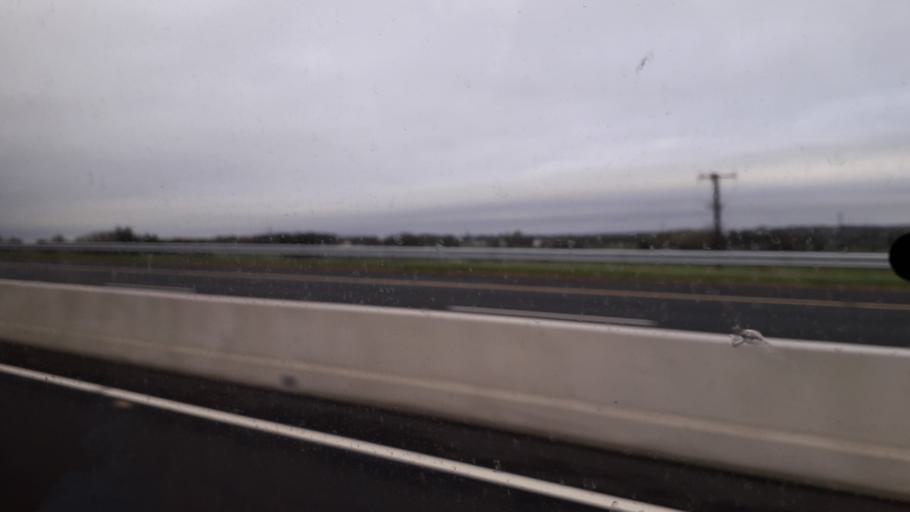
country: IE
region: Connaught
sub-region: County Galway
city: Athenry
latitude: 53.2781
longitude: -8.8018
